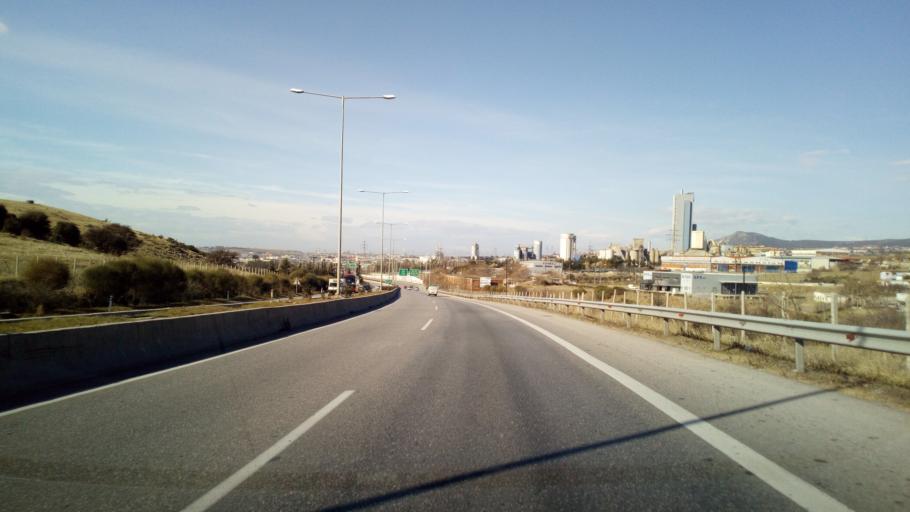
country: GR
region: Central Macedonia
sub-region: Nomos Thessalonikis
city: Efkarpia
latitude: 40.6944
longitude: 22.9628
